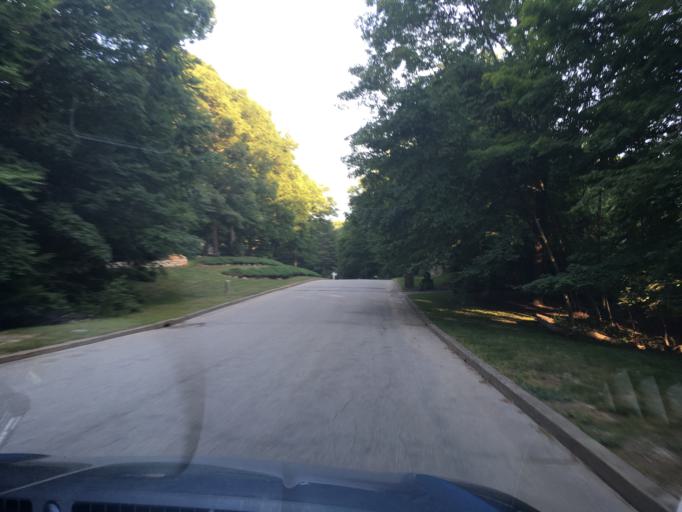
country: US
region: Rhode Island
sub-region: Washington County
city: Exeter
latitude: 41.6348
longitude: -71.5179
